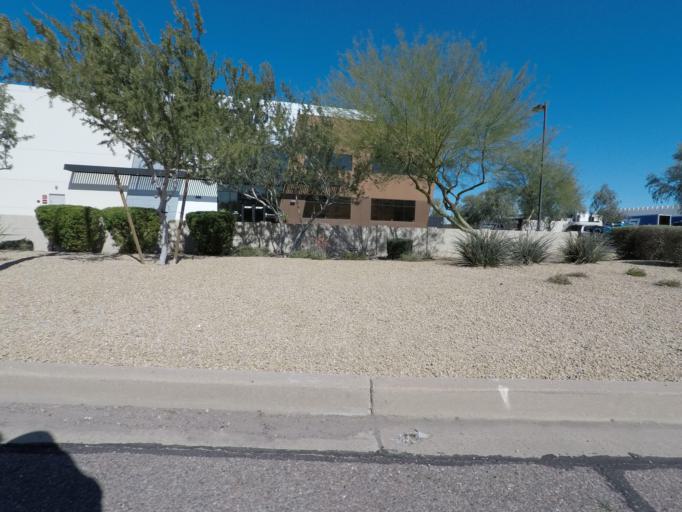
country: US
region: Arizona
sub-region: Maricopa County
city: Tempe Junction
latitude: 33.4134
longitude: -111.9947
